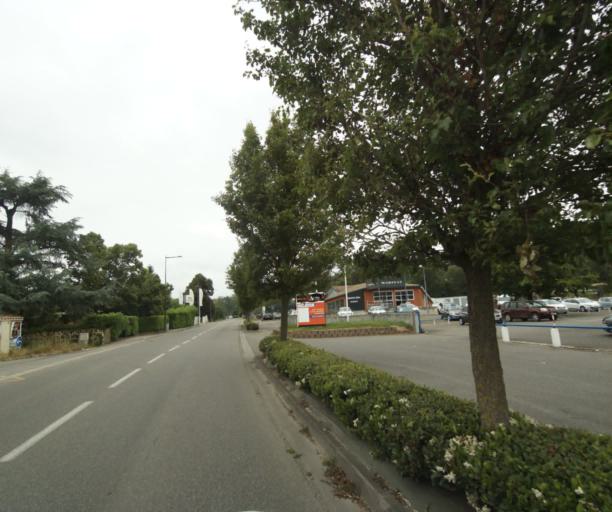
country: FR
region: Midi-Pyrenees
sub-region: Departement du Tarn-et-Garonne
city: Montauban
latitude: 44.0063
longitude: 1.3559
